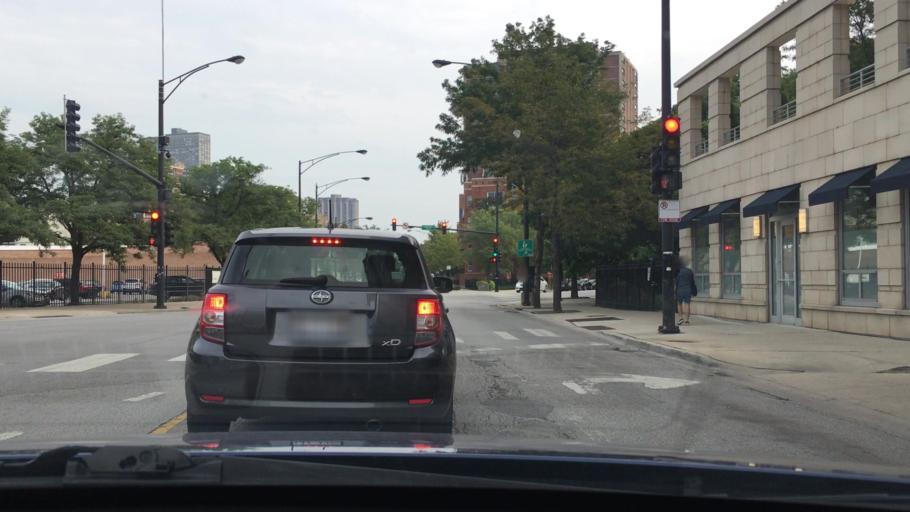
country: US
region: Illinois
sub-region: Cook County
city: Lincolnwood
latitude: 41.9615
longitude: -87.6550
